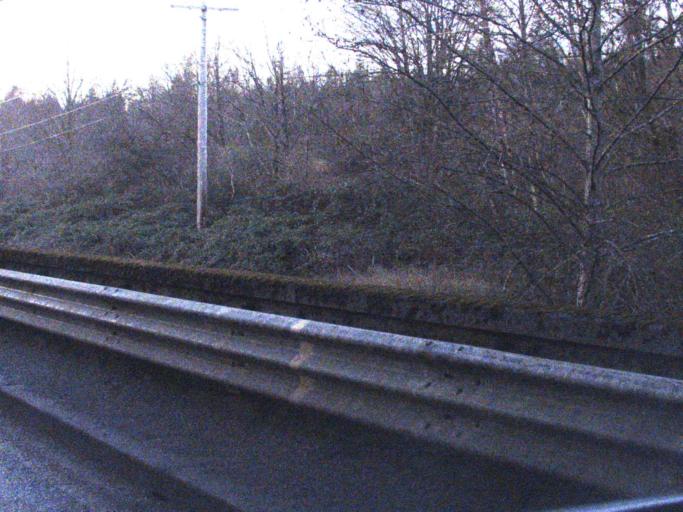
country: US
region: Washington
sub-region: Skagit County
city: Sedro-Woolley
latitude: 48.5326
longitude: -121.8845
